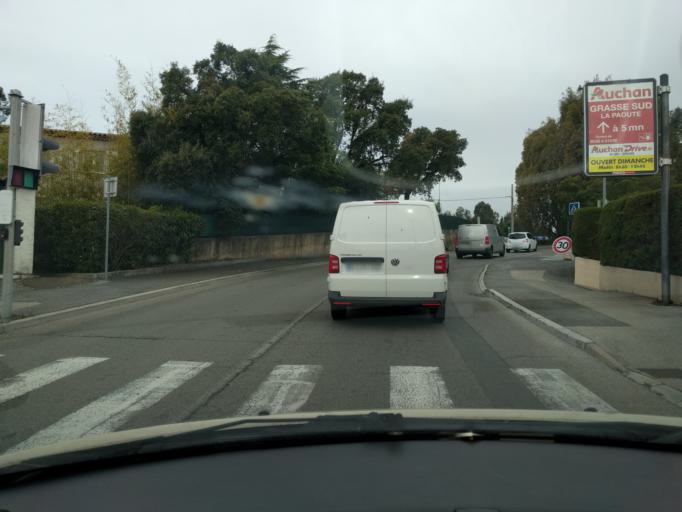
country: FR
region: Provence-Alpes-Cote d'Azur
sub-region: Departement des Alpes-Maritimes
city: La Roquette-sur-Siagne
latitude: 43.5965
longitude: 6.9554
